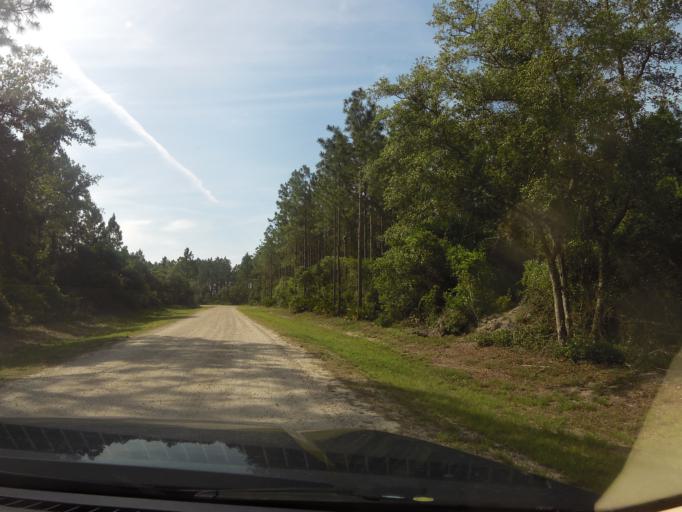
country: US
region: Florida
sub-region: Nassau County
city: Fernandina Beach
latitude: 30.4971
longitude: -81.4933
